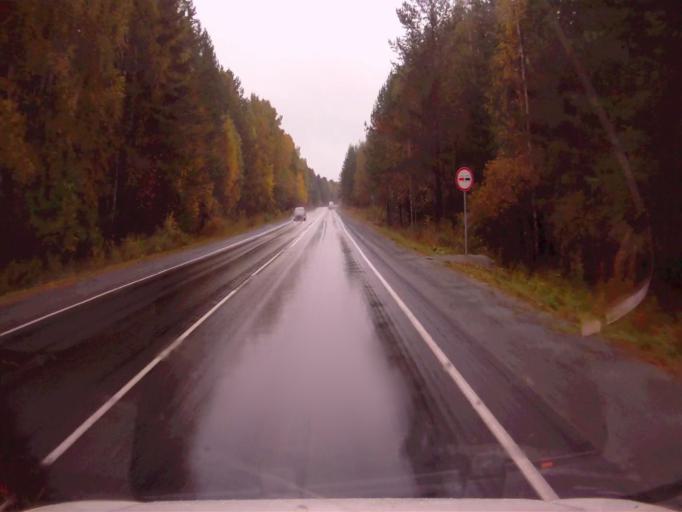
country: RU
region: Chelyabinsk
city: Tayginka
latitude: 55.5525
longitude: 60.6463
